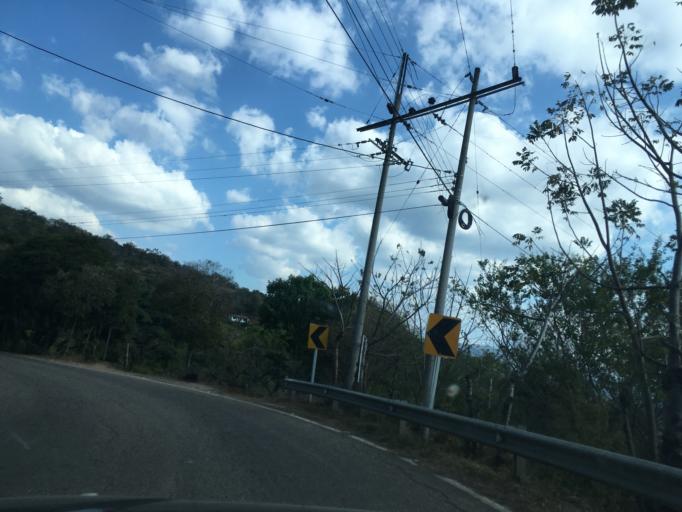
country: CO
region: Santander
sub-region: San Gil
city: San Gil
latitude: 6.5743
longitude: -73.1514
